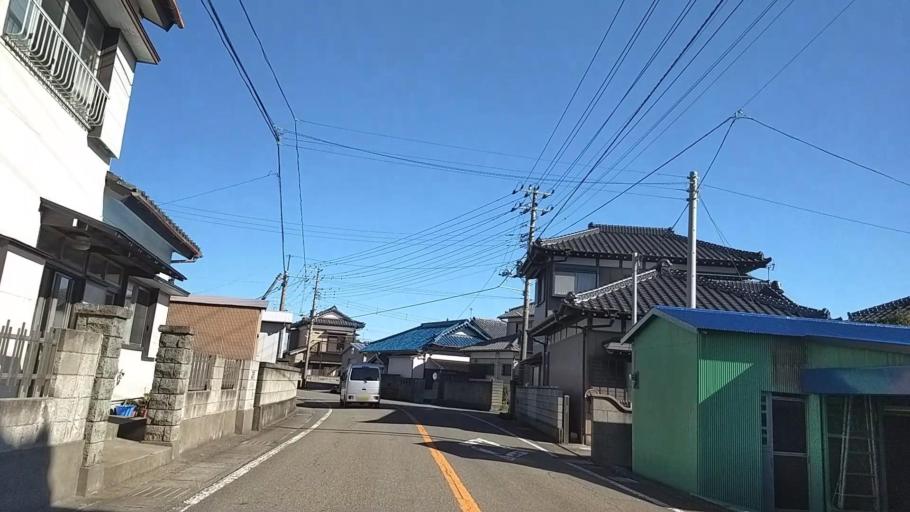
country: JP
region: Chiba
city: Tateyama
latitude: 34.9360
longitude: 139.9517
